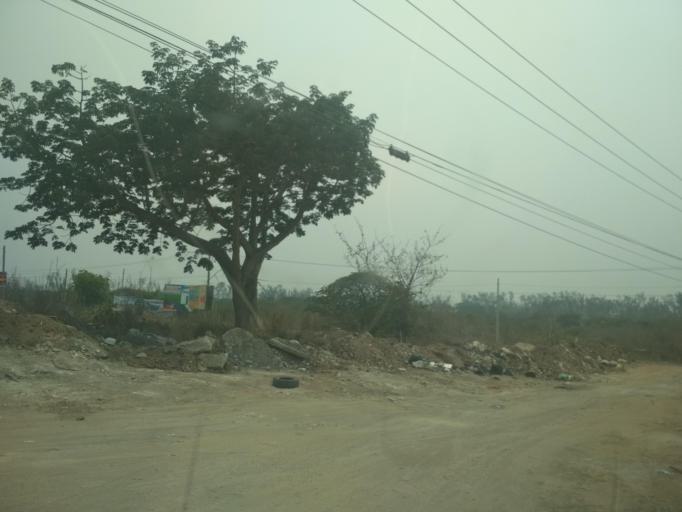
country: MX
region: Veracruz
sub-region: Veracruz
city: Las Amapolas
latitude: 19.1511
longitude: -96.2188
